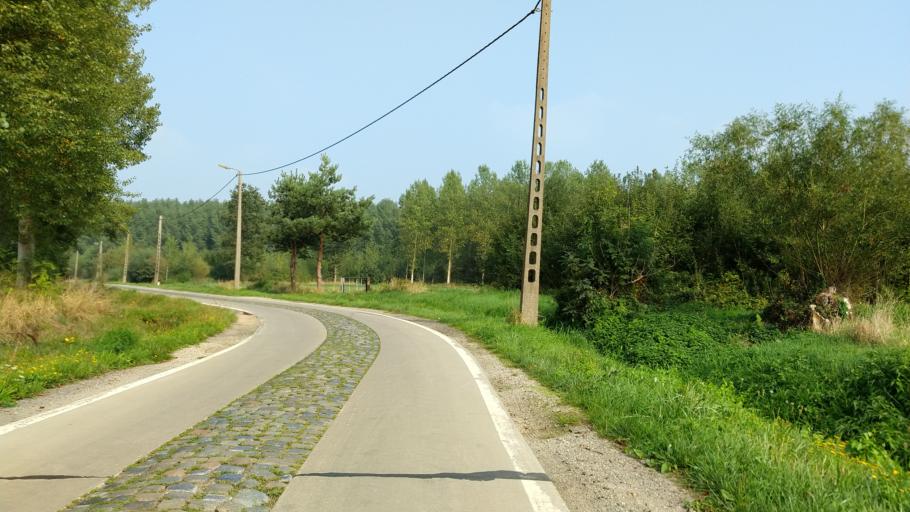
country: BE
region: Flanders
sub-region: Provincie Vlaams-Brabant
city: Rotselaar
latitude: 50.9553
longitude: 4.6859
